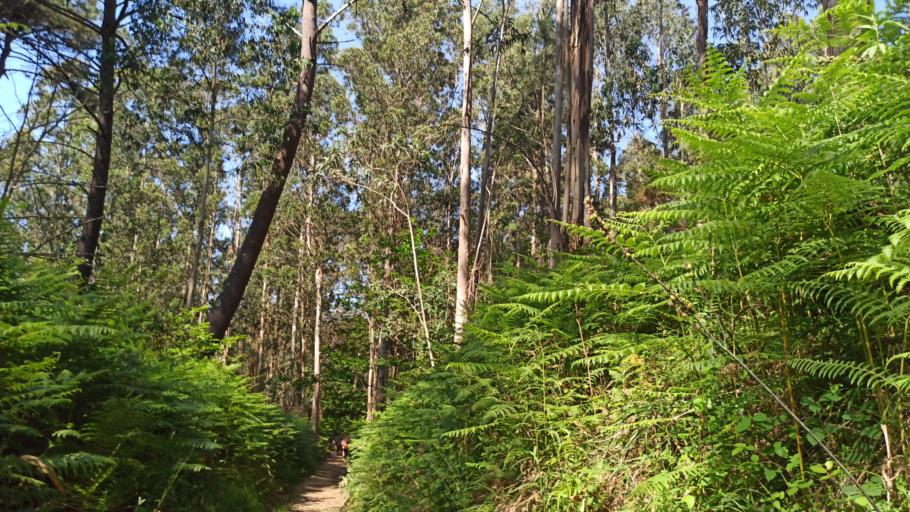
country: ES
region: Galicia
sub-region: Provincia da Coruna
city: Sada
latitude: 43.3819
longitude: -8.2712
